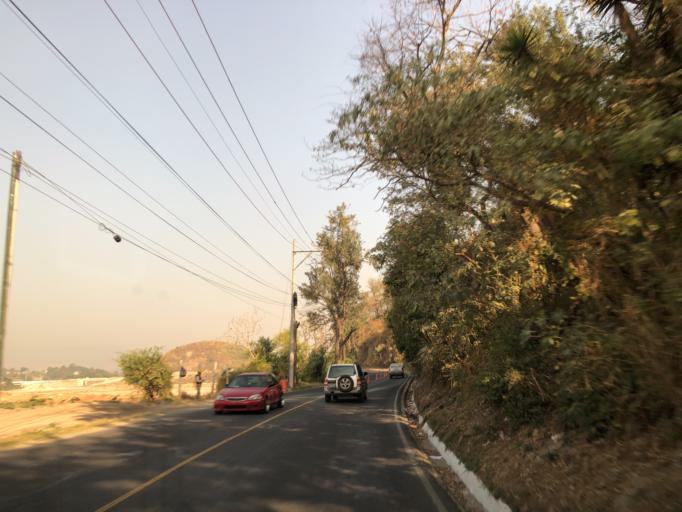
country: GT
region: Guatemala
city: Petapa
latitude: 14.4954
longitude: -90.5407
